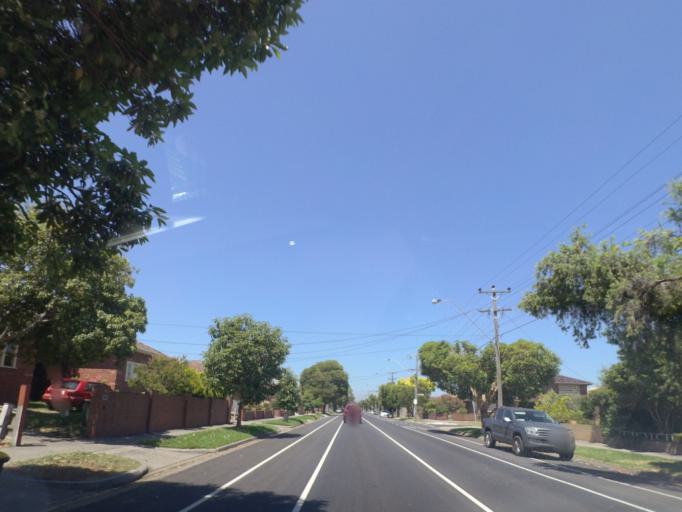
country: AU
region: Victoria
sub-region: Moreland
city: Pascoe Vale South
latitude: -37.7320
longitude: 144.9433
